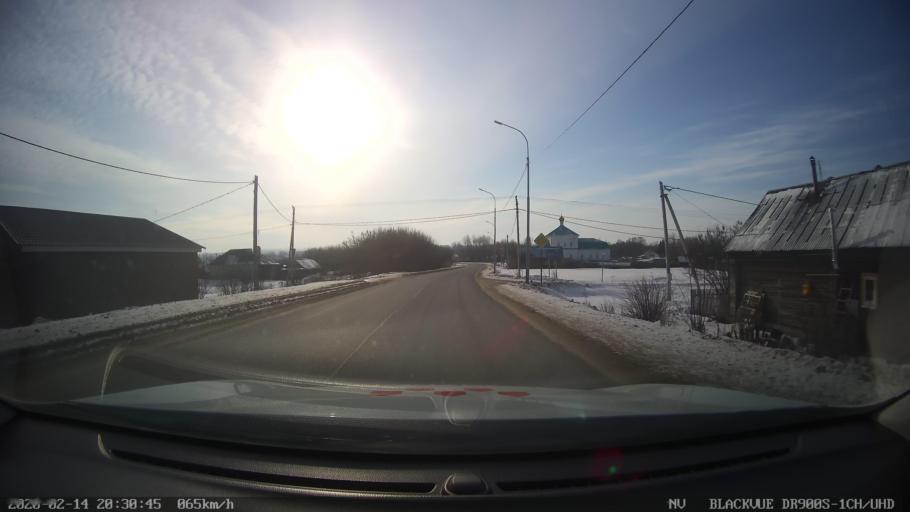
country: RU
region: Tatarstan
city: Stolbishchi
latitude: 55.4407
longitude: 48.9918
